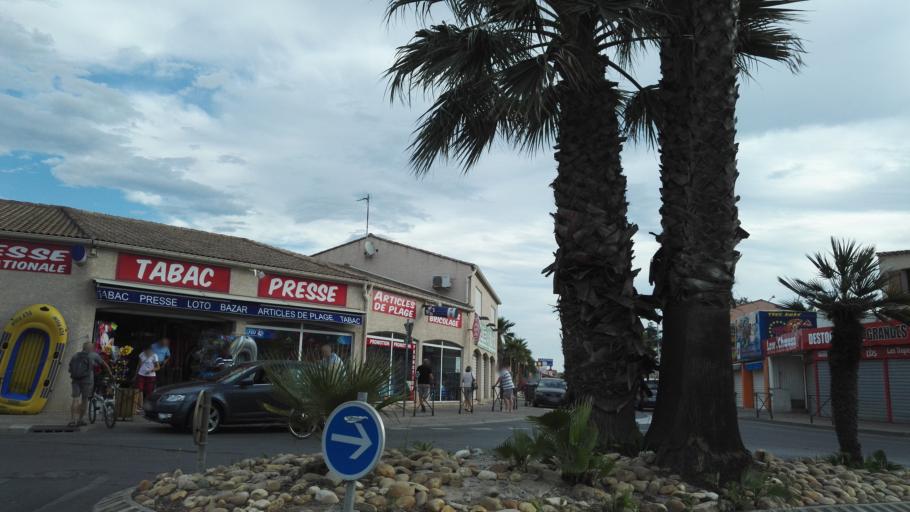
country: FR
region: Languedoc-Roussillon
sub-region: Departement de l'Herault
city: Le Cap d'Agde
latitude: 43.3108
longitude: 3.5439
